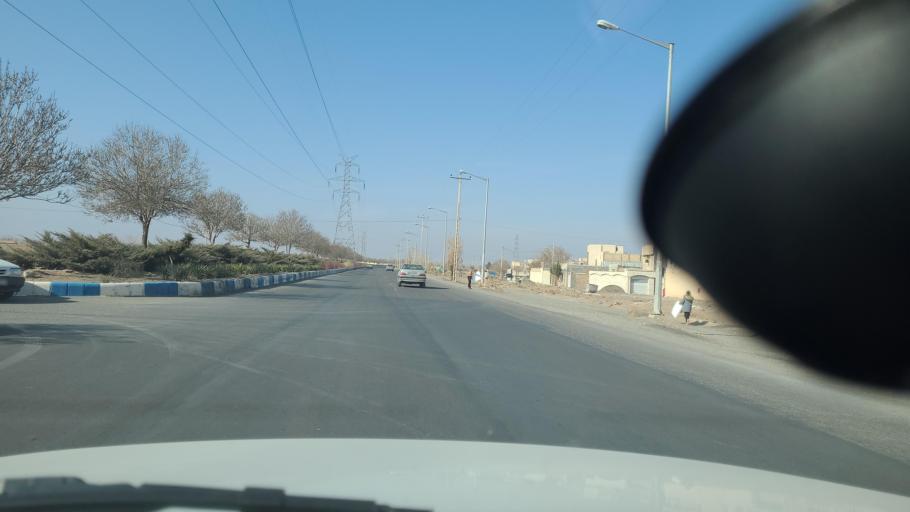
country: IR
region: Razavi Khorasan
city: Fariman
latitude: 35.6973
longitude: 59.8397
